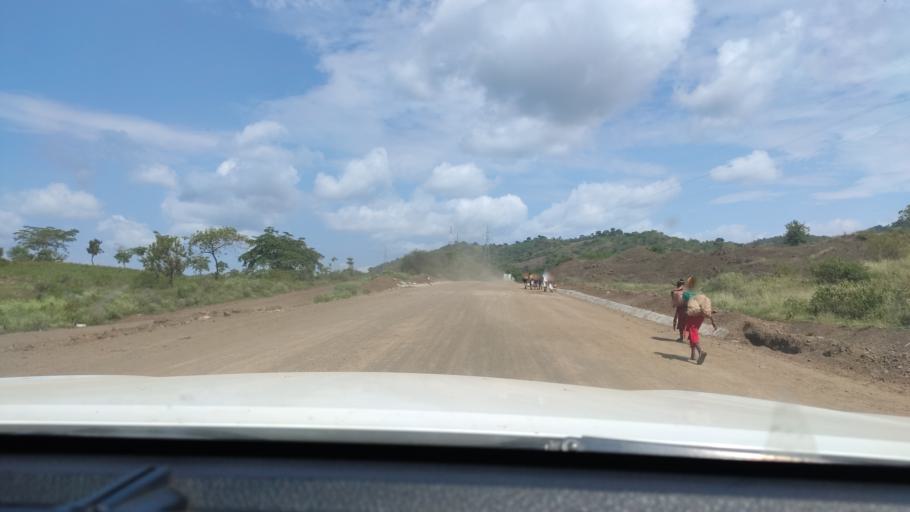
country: ET
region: Southern Nations, Nationalities, and People's Region
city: Felege Neway
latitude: 6.3914
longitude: 37.0588
